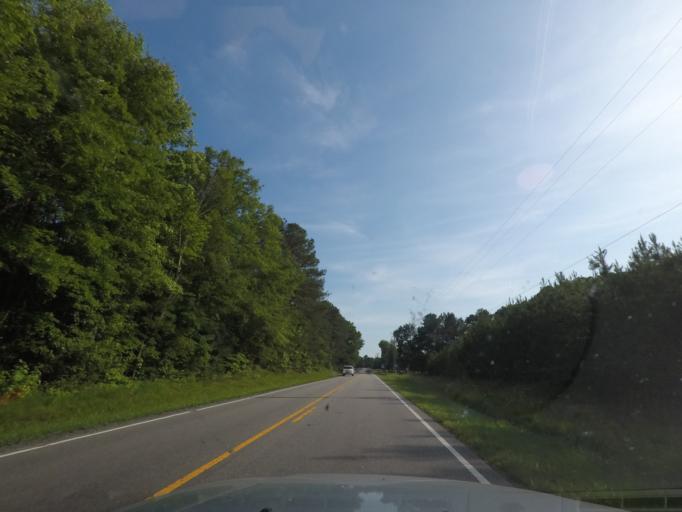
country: US
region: North Carolina
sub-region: Granville County
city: Oxford
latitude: 36.4564
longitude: -78.5655
